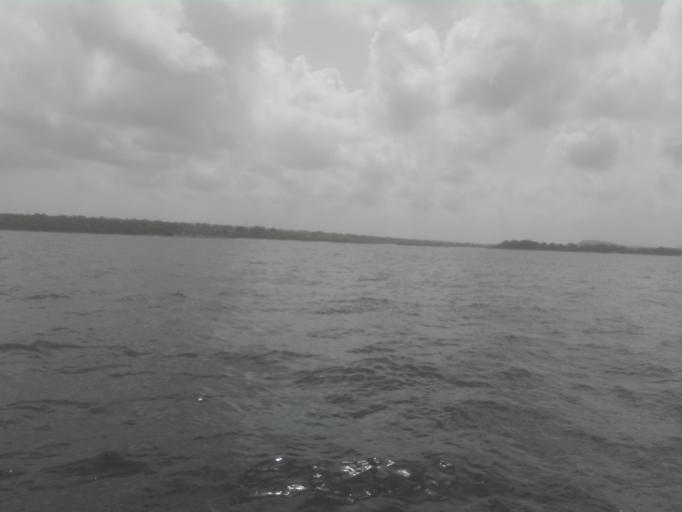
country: CO
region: Bolivar
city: Turbana
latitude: 10.2347
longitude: -75.6145
